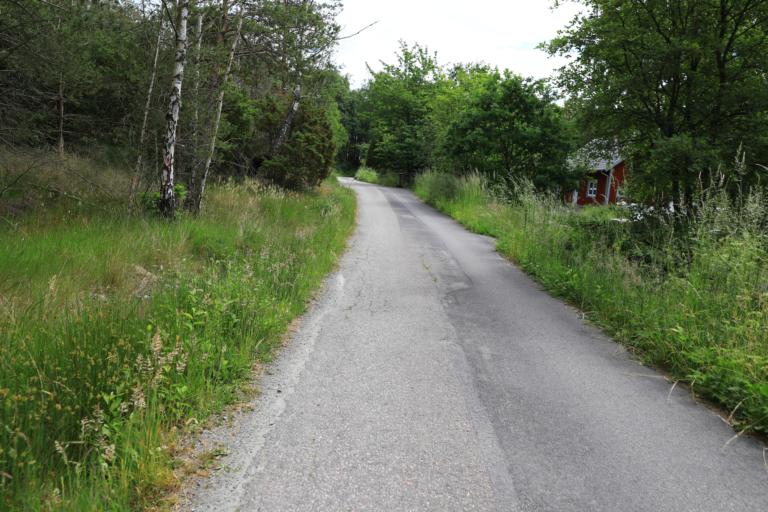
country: SE
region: Halland
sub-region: Varbergs Kommun
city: Varberg
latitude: 57.1669
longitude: 12.2485
